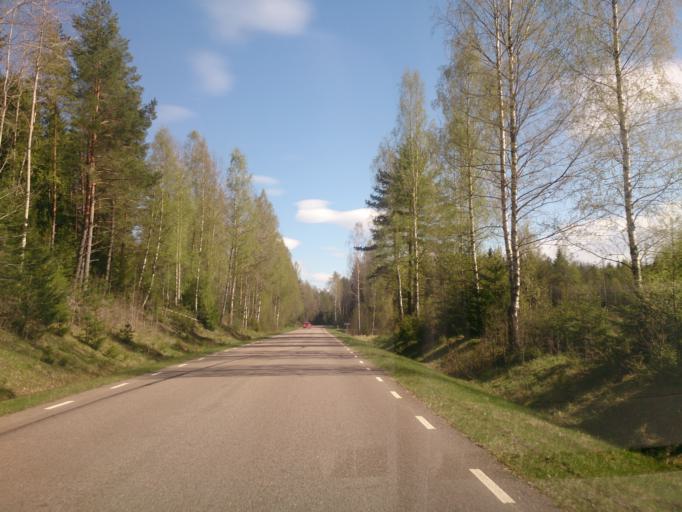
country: SE
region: OEstergoetland
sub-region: Linkopings Kommun
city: Ljungsbro
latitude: 58.6005
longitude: 15.4901
